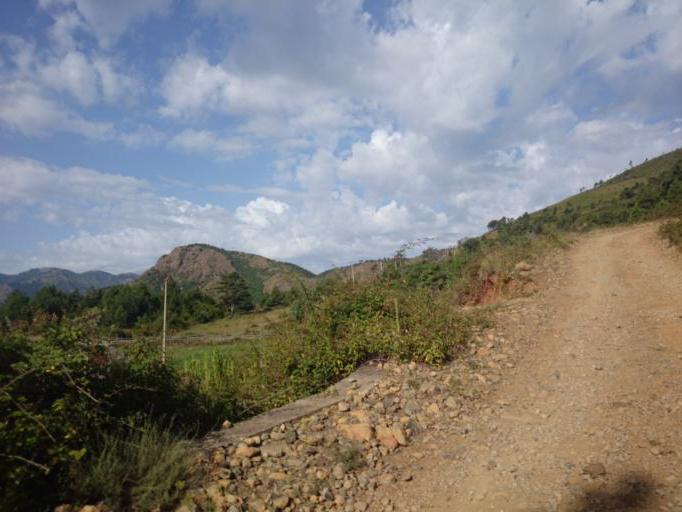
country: AL
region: Elbasan
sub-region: Rrethi i Gramshit
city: Lenias
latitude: 40.7748
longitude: 20.3552
